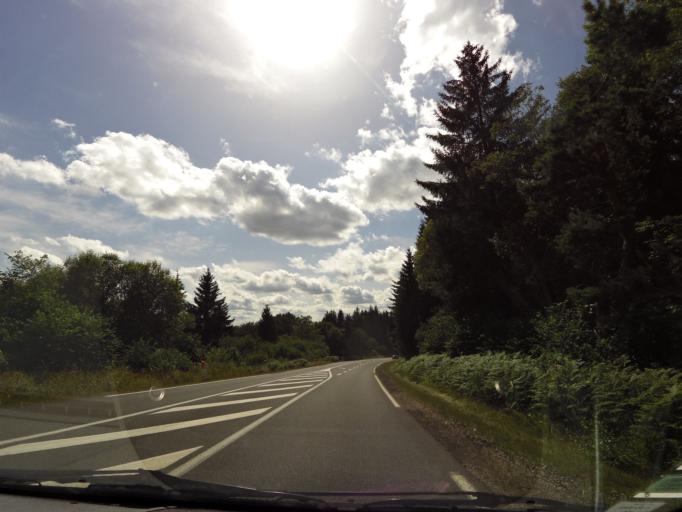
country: FR
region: Auvergne
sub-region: Departement du Puy-de-Dome
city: Aydat
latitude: 45.7345
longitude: 2.9300
